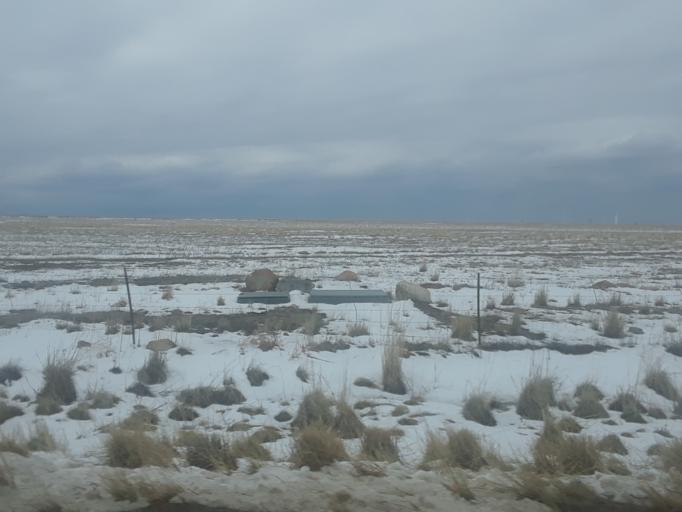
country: US
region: Colorado
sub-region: Jefferson County
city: Golden
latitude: 39.8666
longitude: -105.2479
